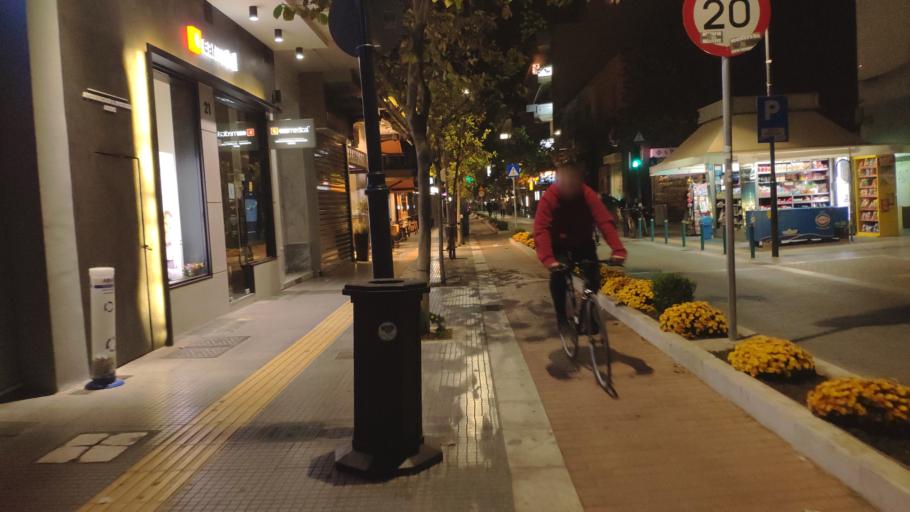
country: GR
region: Thessaly
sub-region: Nomos Larisis
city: Larisa
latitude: 39.6374
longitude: 22.4167
